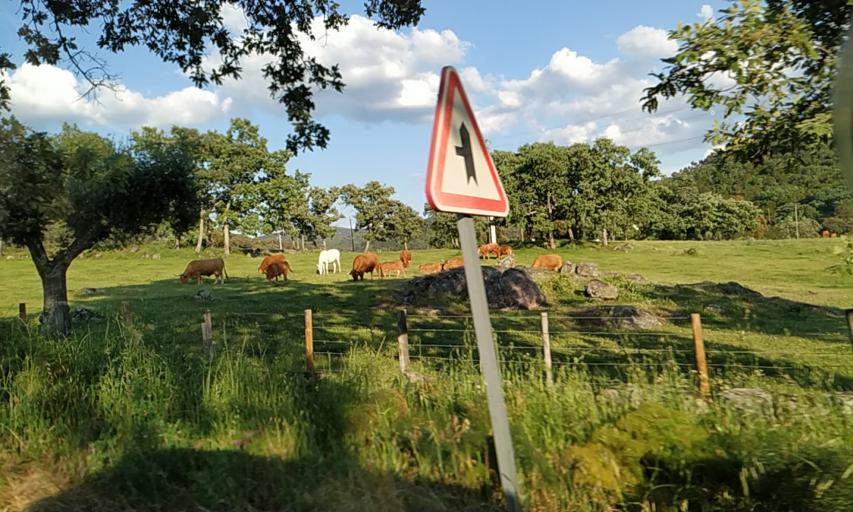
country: PT
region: Portalegre
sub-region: Portalegre
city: Portalegre
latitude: 39.3275
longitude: -7.4331
